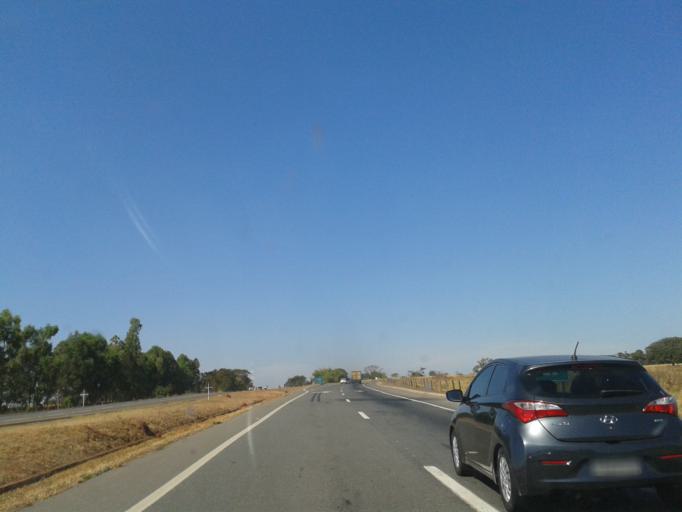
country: BR
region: Goias
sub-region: Piracanjuba
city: Piracanjuba
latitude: -17.2817
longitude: -49.2363
